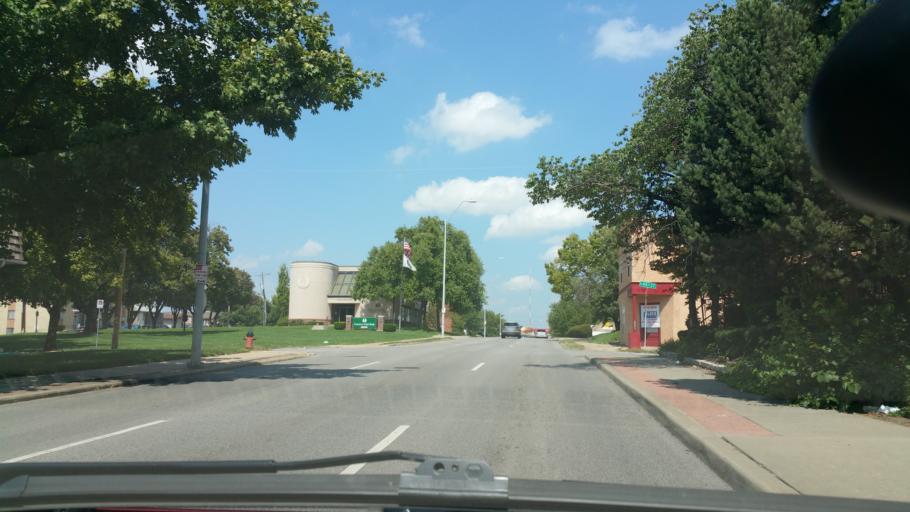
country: US
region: Kansas
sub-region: Johnson County
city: Westwood
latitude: 39.0477
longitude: -94.5970
